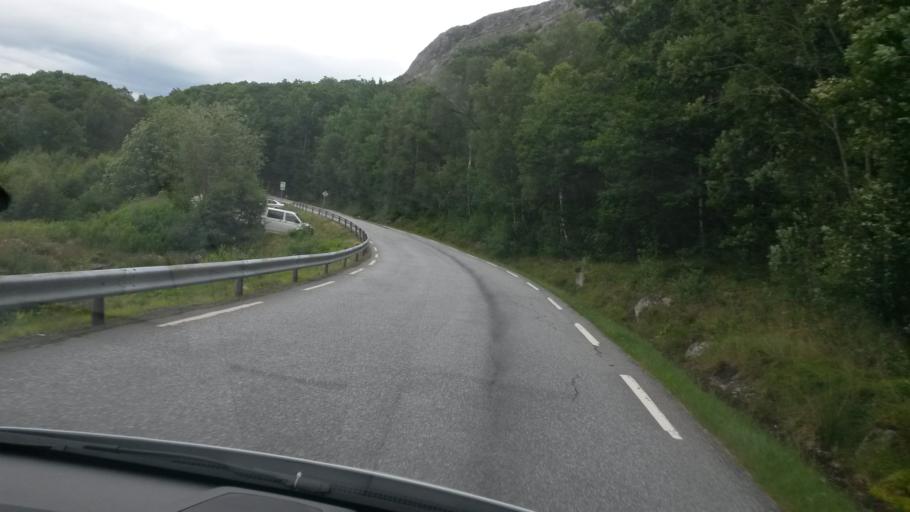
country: NO
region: Rogaland
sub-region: Sandnes
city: Sandnes
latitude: 58.8860
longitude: 5.7768
